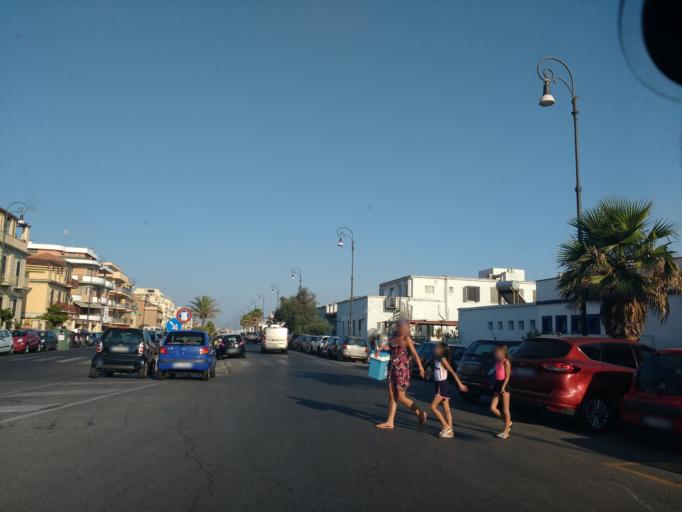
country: IT
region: Latium
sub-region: Citta metropolitana di Roma Capitale
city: Lido di Ostia
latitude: 41.7309
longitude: 12.2727
